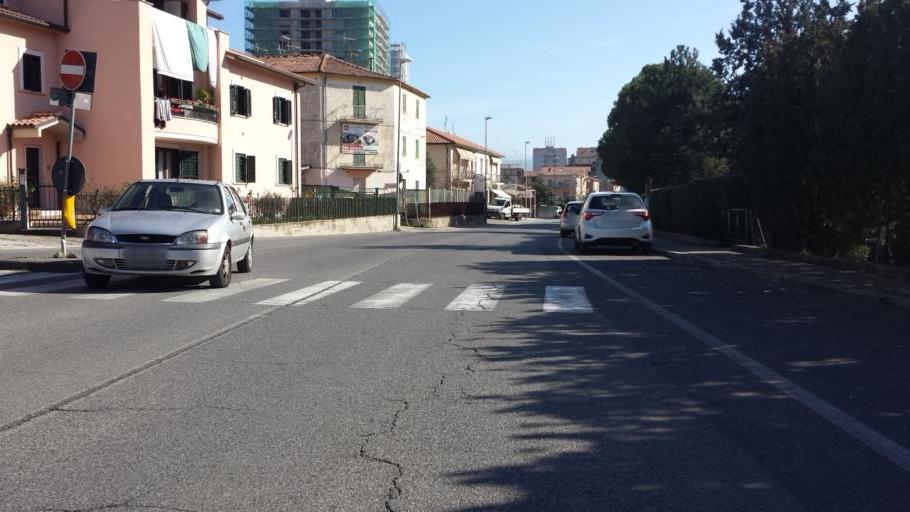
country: IT
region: Umbria
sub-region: Provincia di Terni
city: Terni
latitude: 42.5877
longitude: 12.6069
